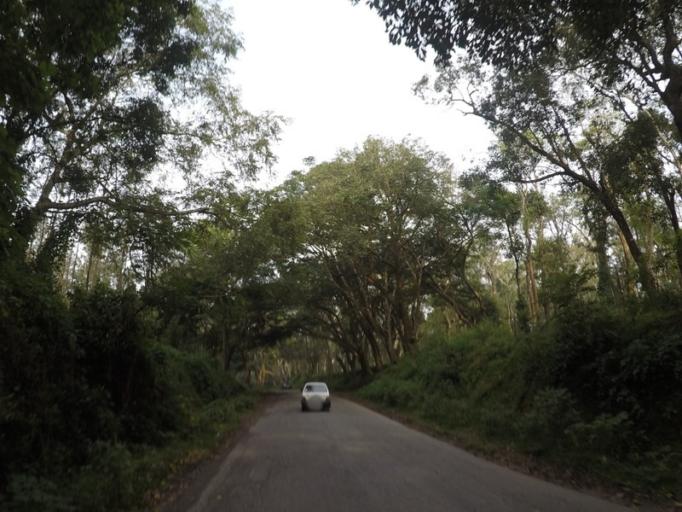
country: IN
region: Karnataka
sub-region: Chikmagalur
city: Chikmagalur
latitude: 13.2696
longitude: 75.6960
